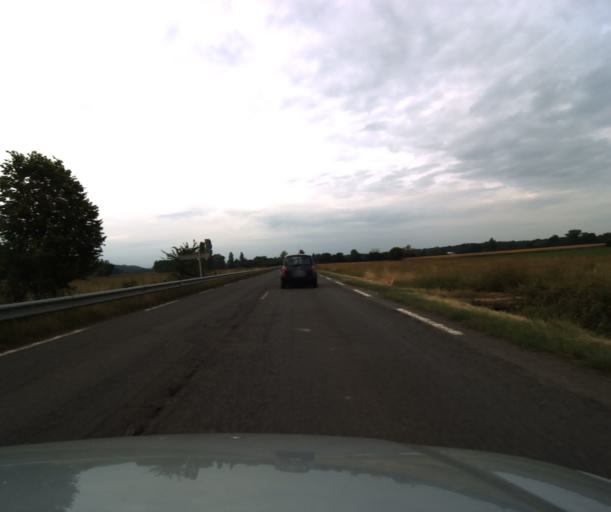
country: FR
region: Midi-Pyrenees
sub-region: Departement des Hautes-Pyrenees
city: Rabastens-de-Bigorre
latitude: 43.3479
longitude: 0.1357
